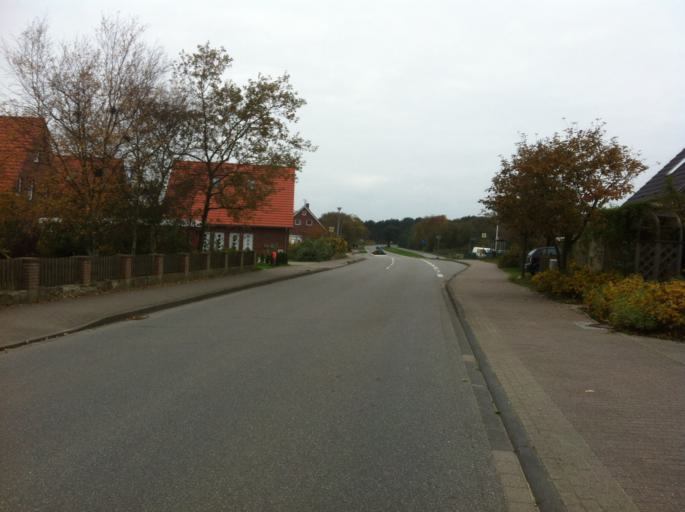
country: DE
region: Schleswig-Holstein
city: Wittdun
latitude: 54.6273
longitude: 8.3854
